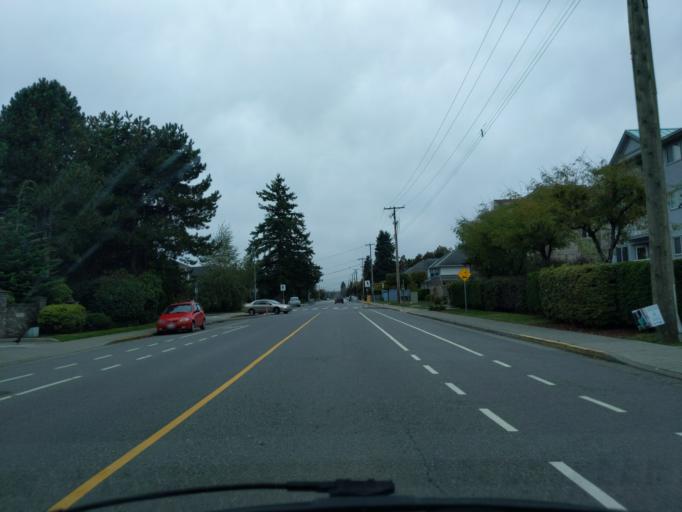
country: CA
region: British Columbia
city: Pitt Meadows
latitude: 49.2224
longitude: -122.6931
